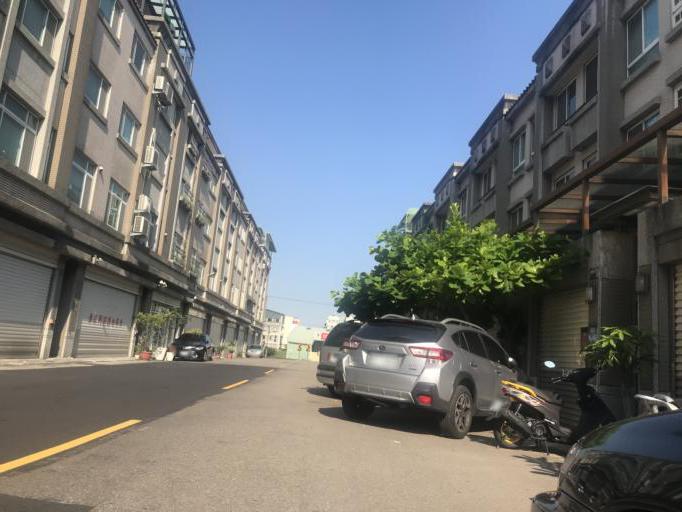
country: TW
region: Taiwan
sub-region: Taichung City
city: Taichung
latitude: 24.1100
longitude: 120.6568
